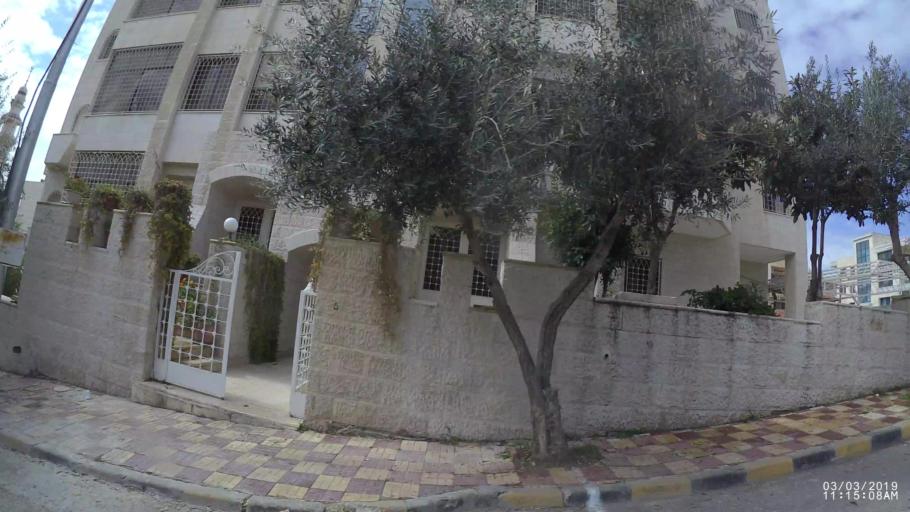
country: JO
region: Amman
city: Amman
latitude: 31.9975
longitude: 35.9132
